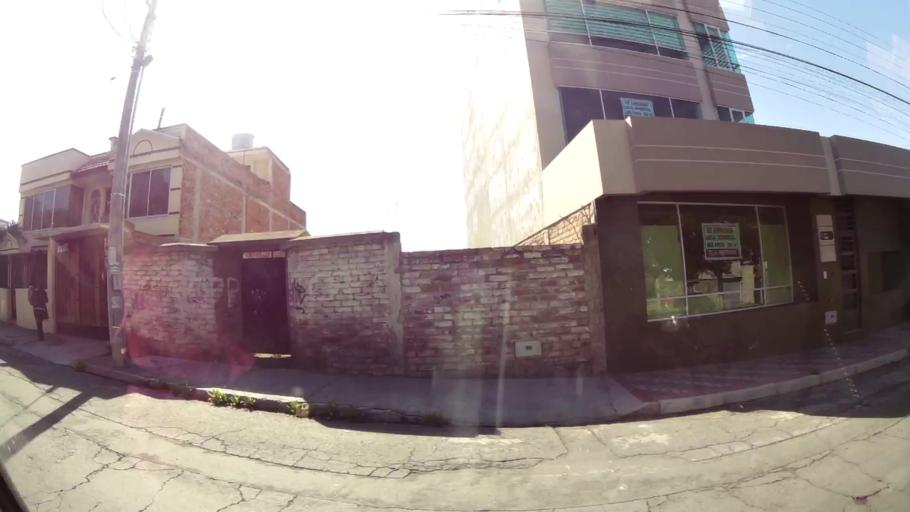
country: EC
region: Chimborazo
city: Riobamba
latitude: -1.6580
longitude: -78.6670
